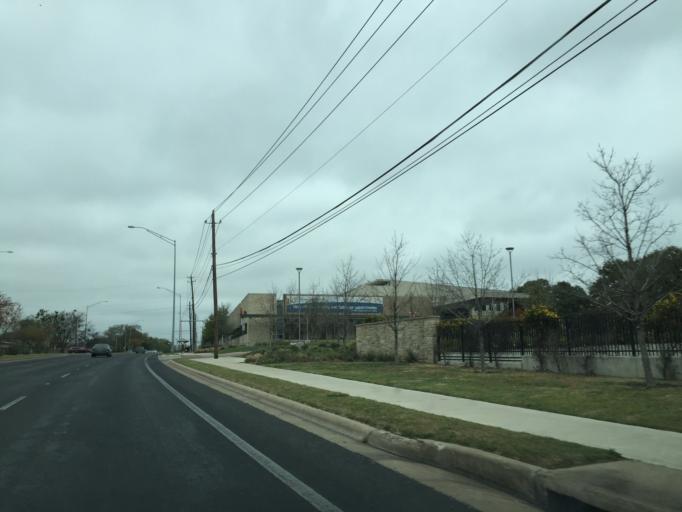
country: US
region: Texas
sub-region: Travis County
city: Wells Branch
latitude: 30.3849
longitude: -97.6929
